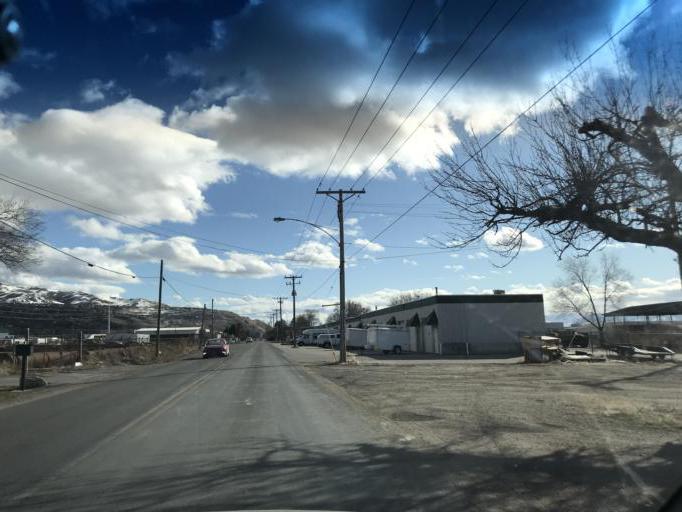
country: US
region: Utah
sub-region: Davis County
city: North Salt Lake
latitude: 40.8665
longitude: -111.9119
